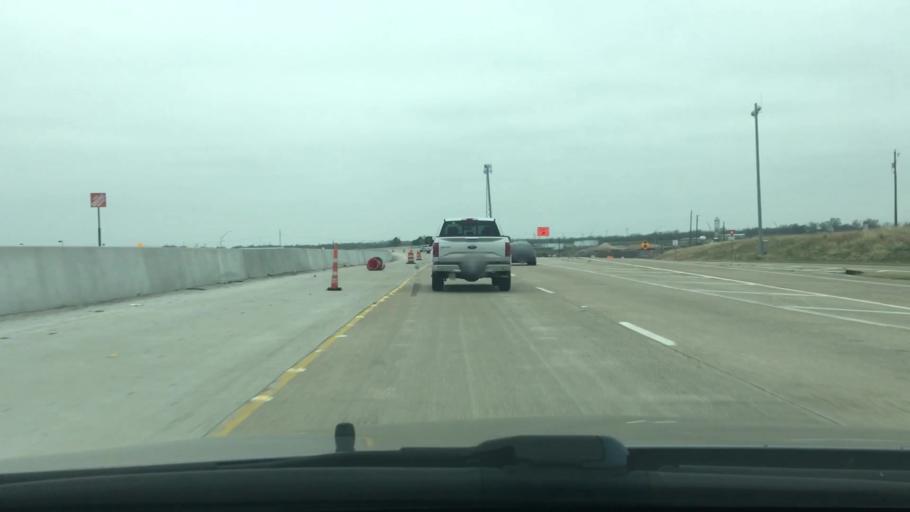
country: US
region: Texas
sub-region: Navarro County
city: Corsicana
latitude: 32.0683
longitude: -96.4504
